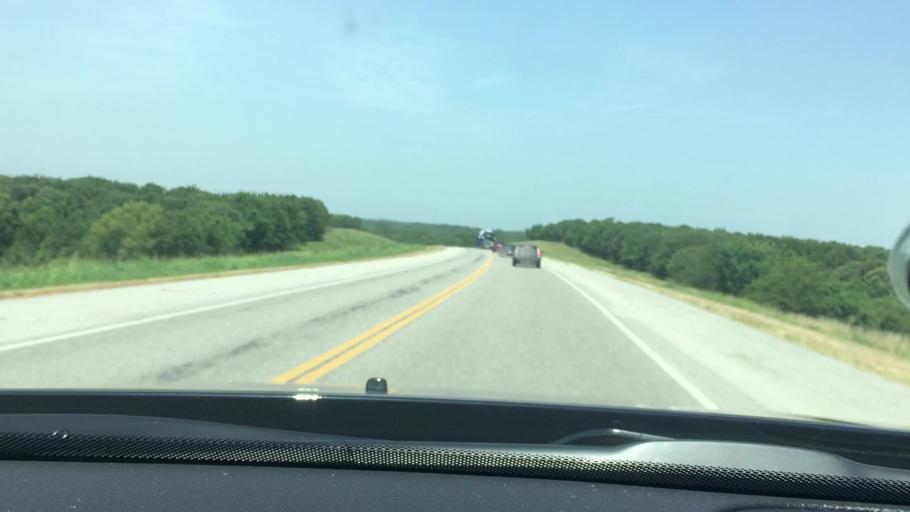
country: US
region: Oklahoma
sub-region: Coal County
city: Coalgate
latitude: 34.6104
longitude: -96.3848
